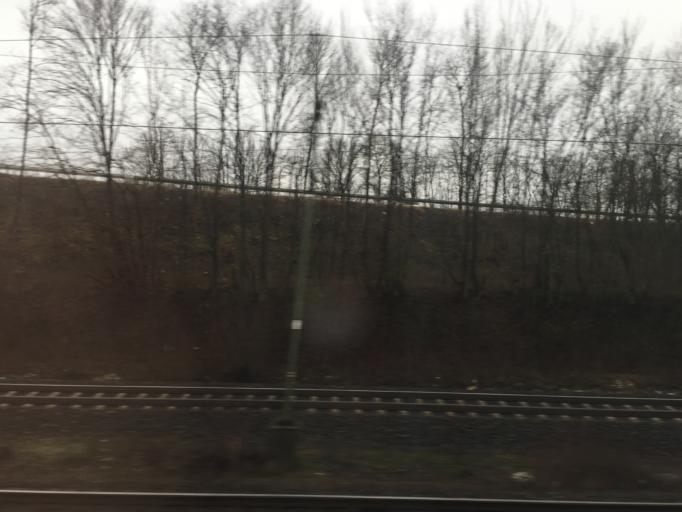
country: DE
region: Baden-Wuerttemberg
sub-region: Regierungsbezirk Stuttgart
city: Asperg
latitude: 48.9203
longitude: 9.1344
